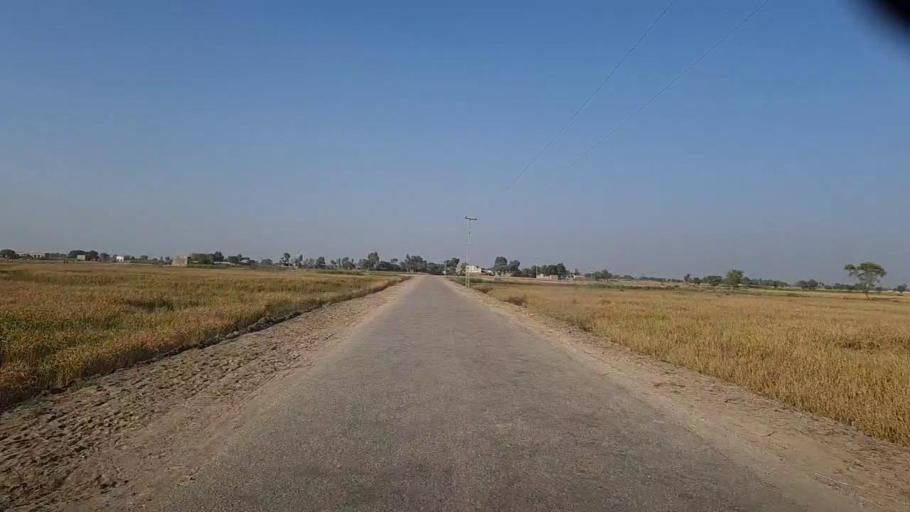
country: PK
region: Sindh
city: Tangwani
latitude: 28.2901
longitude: 68.9516
